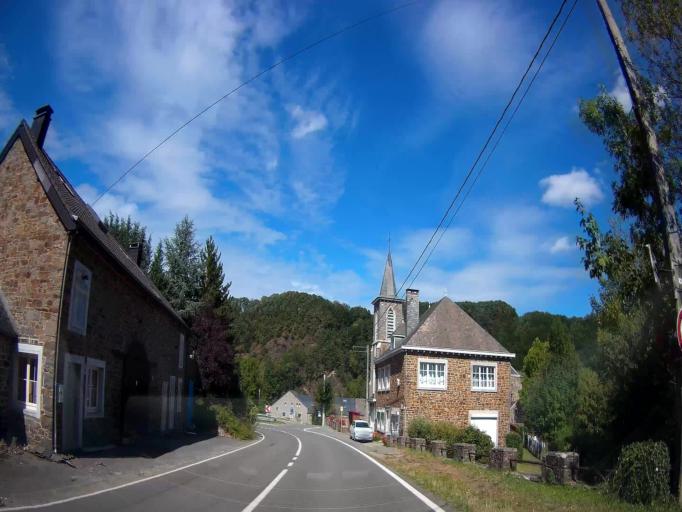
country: BE
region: Wallonia
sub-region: Province du Luxembourg
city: Rendeux
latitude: 50.2074
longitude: 5.5376
